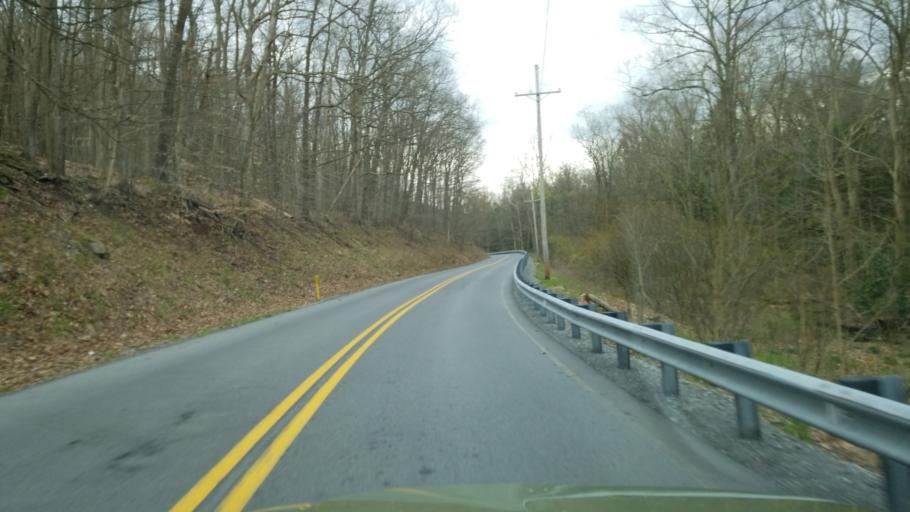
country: US
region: Pennsylvania
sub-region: Blair County
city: Tipton
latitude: 40.6587
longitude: -78.3318
